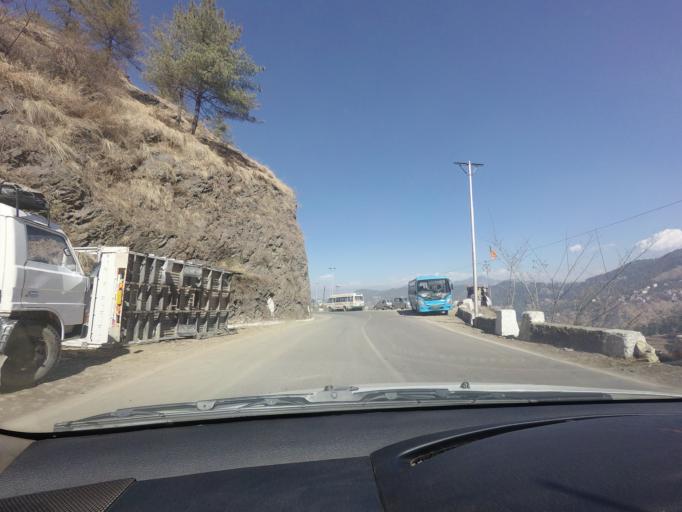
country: IN
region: Himachal Pradesh
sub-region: Shimla
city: Shimla
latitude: 31.1072
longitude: 77.2003
